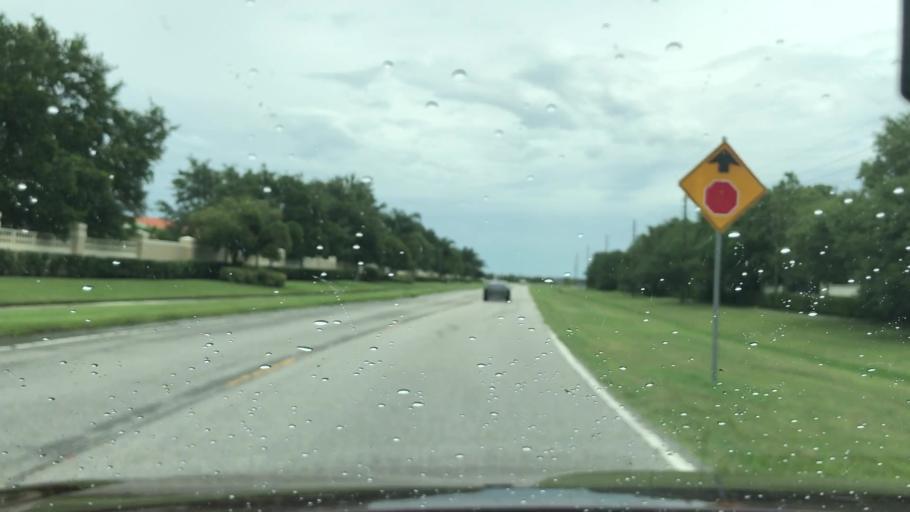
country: US
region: Florida
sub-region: Sarasota County
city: Lake Sarasota
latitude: 27.3099
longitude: -82.3947
